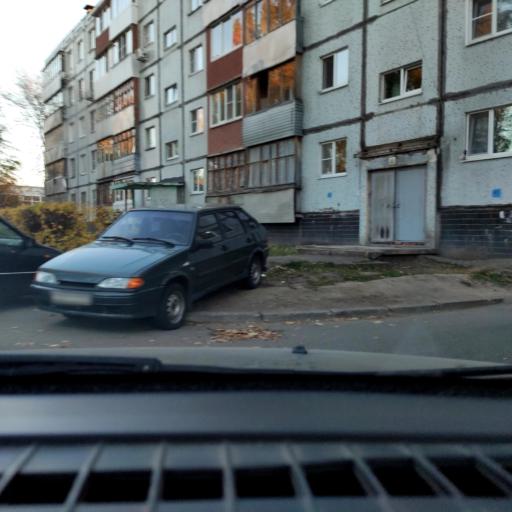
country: RU
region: Samara
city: Tol'yatti
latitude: 53.5239
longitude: 49.2621
